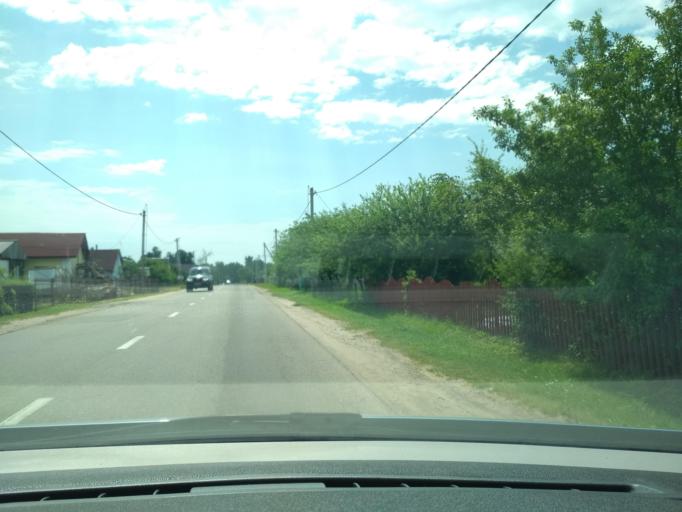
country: BY
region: Grodnenskaya
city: Astravyets
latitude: 54.6120
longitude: 25.9490
